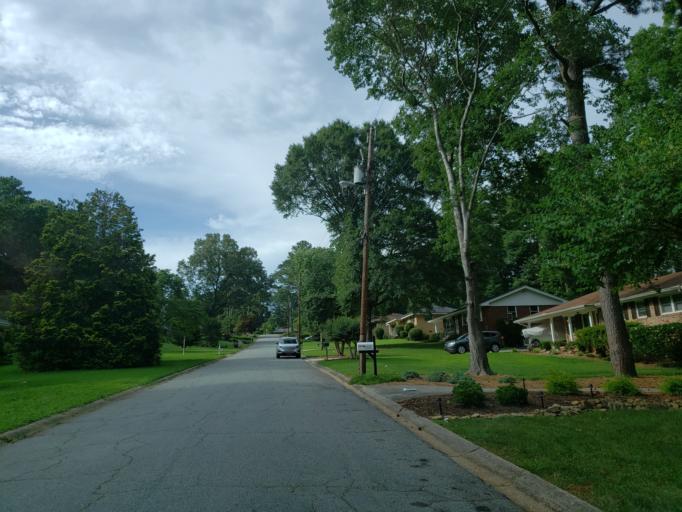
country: US
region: Georgia
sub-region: Cobb County
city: Smyrna
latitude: 33.8582
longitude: -84.5324
